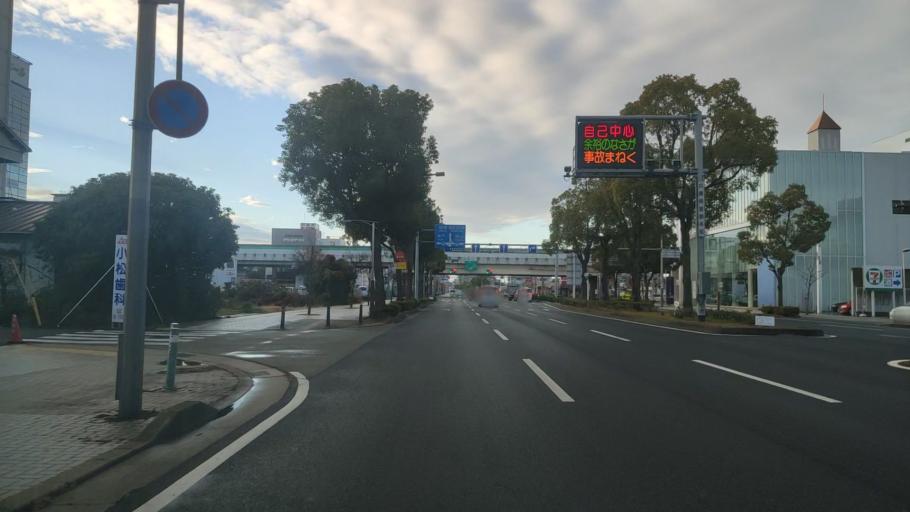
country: JP
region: Hyogo
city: Himeji
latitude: 34.8130
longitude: 134.6832
